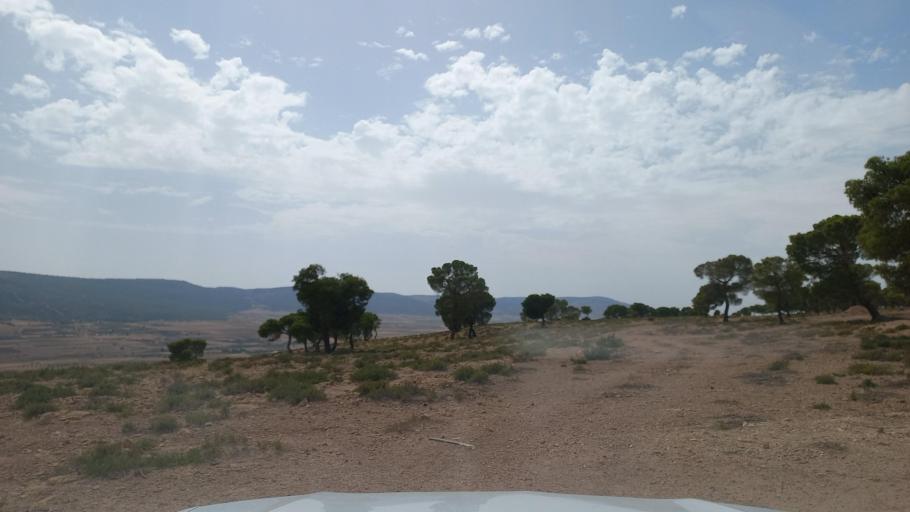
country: TN
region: Al Qasrayn
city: Kasserine
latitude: 35.3763
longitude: 8.8788
